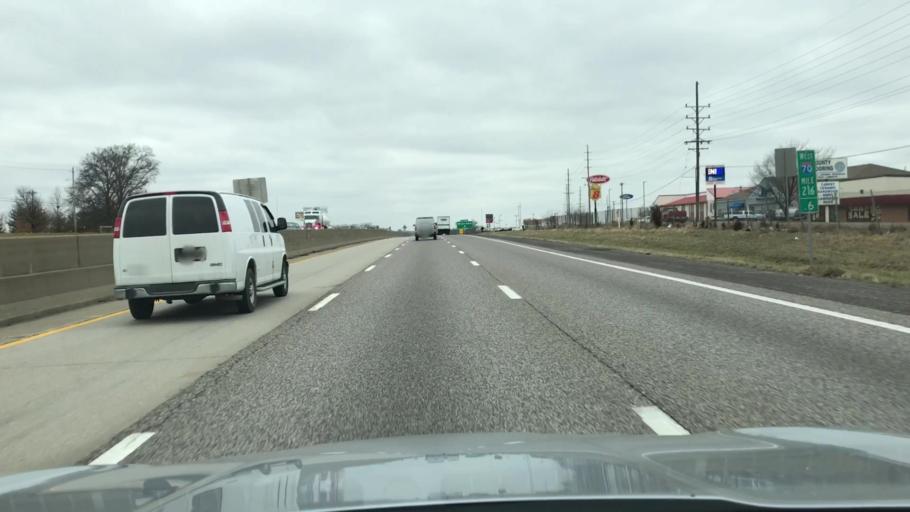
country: US
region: Missouri
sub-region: Saint Charles County
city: O'Fallon
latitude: 38.8024
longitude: -90.7235
